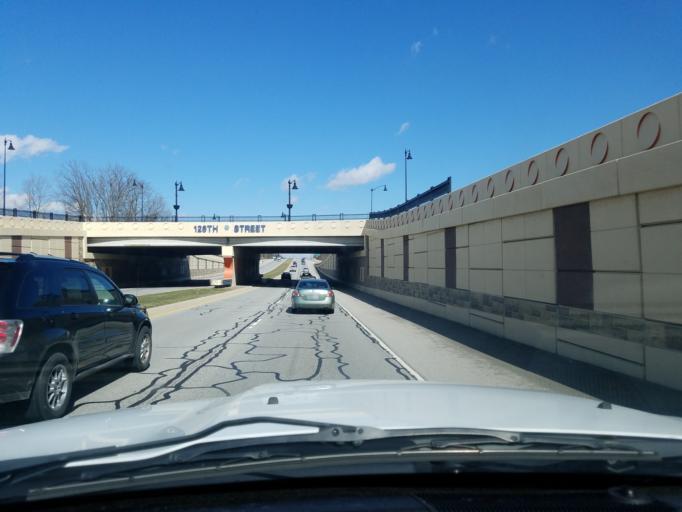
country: US
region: Indiana
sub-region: Hamilton County
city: Carmel
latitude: 39.9703
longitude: -86.1126
